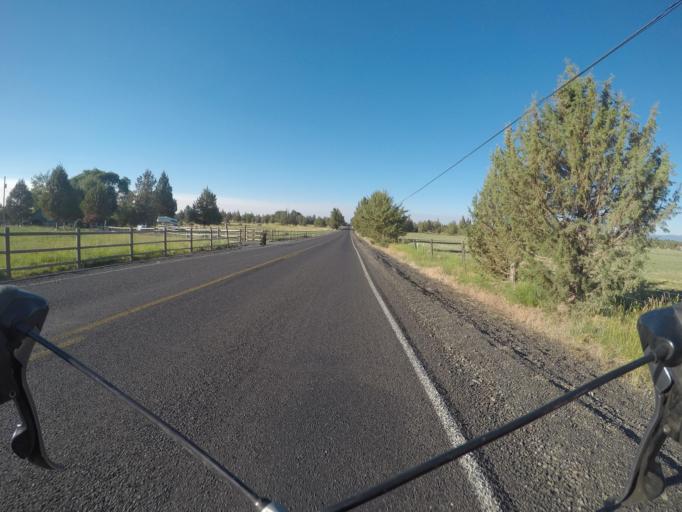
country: US
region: Oregon
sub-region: Deschutes County
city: Redmond
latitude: 44.2616
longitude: -121.2396
